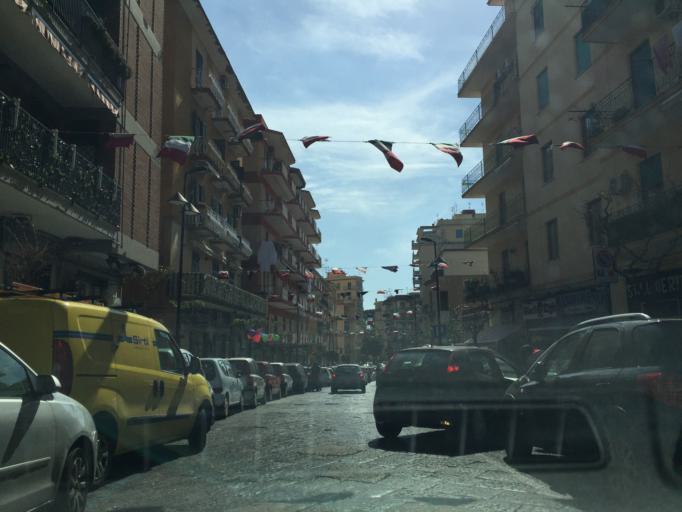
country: IT
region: Campania
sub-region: Provincia di Napoli
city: Ercolano
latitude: 40.8100
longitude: 14.3533
